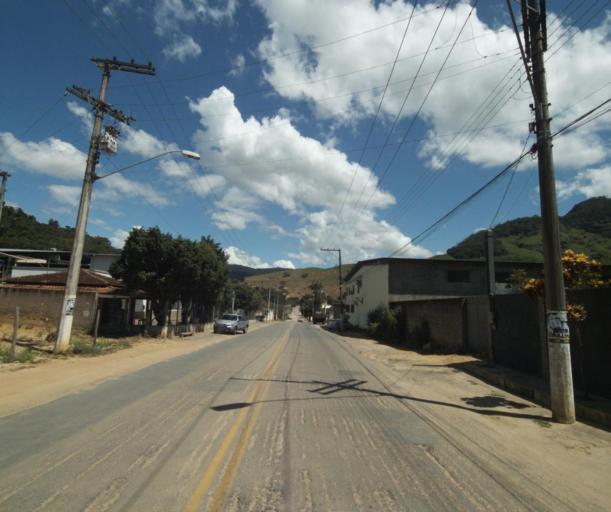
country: BR
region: Espirito Santo
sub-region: Mimoso Do Sul
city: Mimoso do Sul
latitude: -21.0752
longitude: -41.3544
